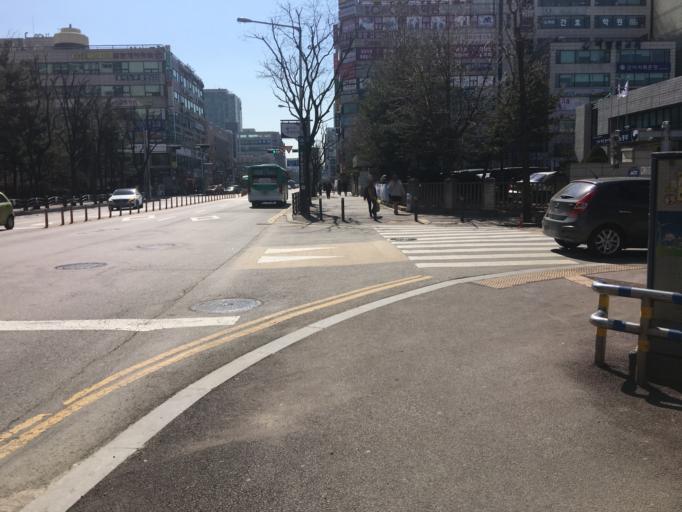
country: KR
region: Gyeonggi-do
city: Bucheon-si
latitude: 37.5063
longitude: 126.7633
